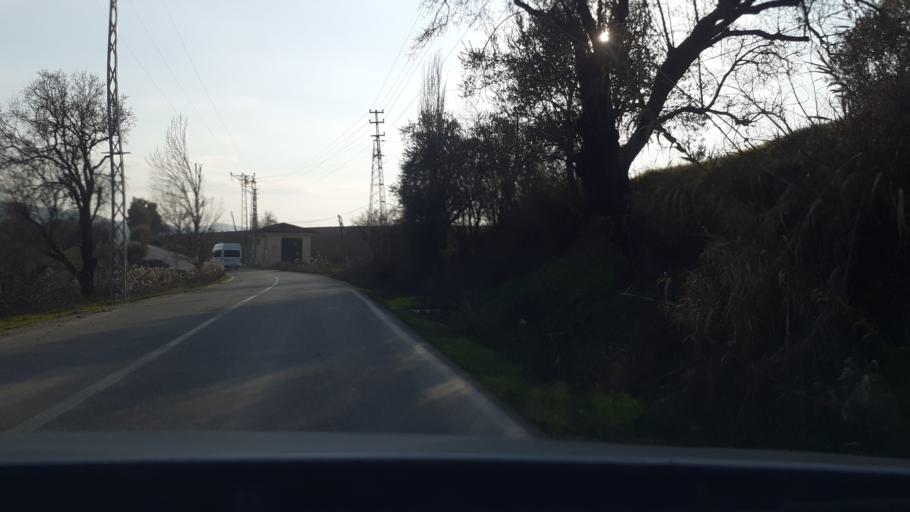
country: TR
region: Hatay
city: Boynuyogun
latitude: 36.1337
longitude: 36.3117
